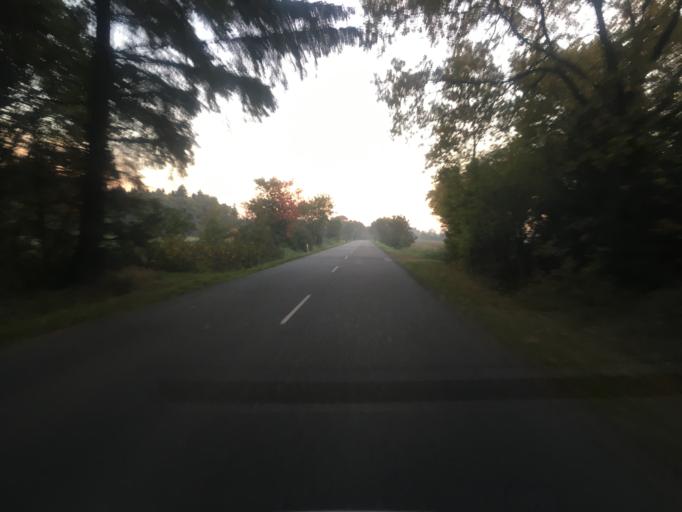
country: DE
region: Schleswig-Holstein
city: Bramstedtlund
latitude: 54.9660
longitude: 9.1176
